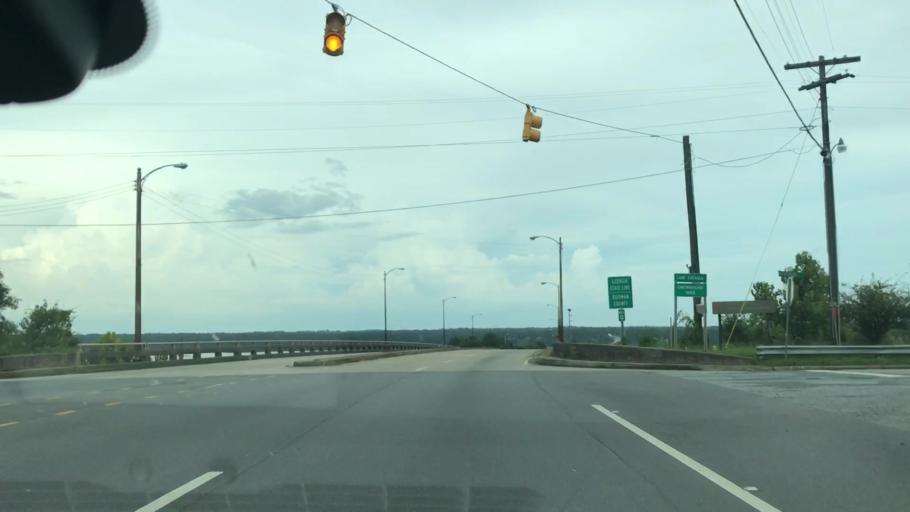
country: US
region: Alabama
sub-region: Barbour County
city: Eufaula
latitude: 31.8914
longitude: -85.1356
